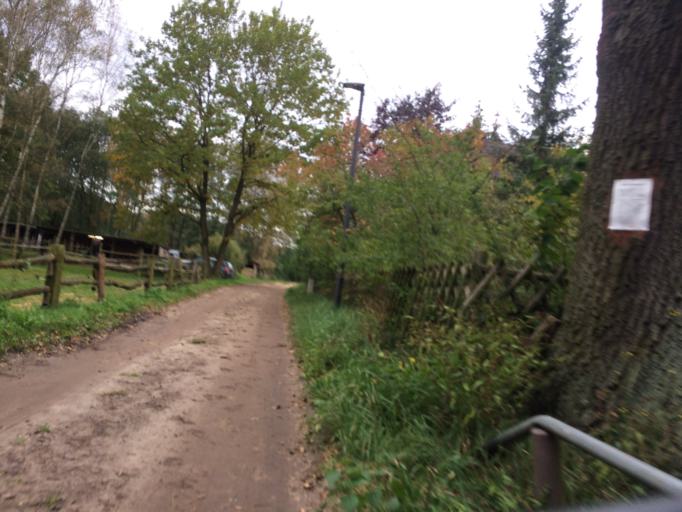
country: DE
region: Brandenburg
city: Glienicke
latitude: 52.6889
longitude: 13.3618
